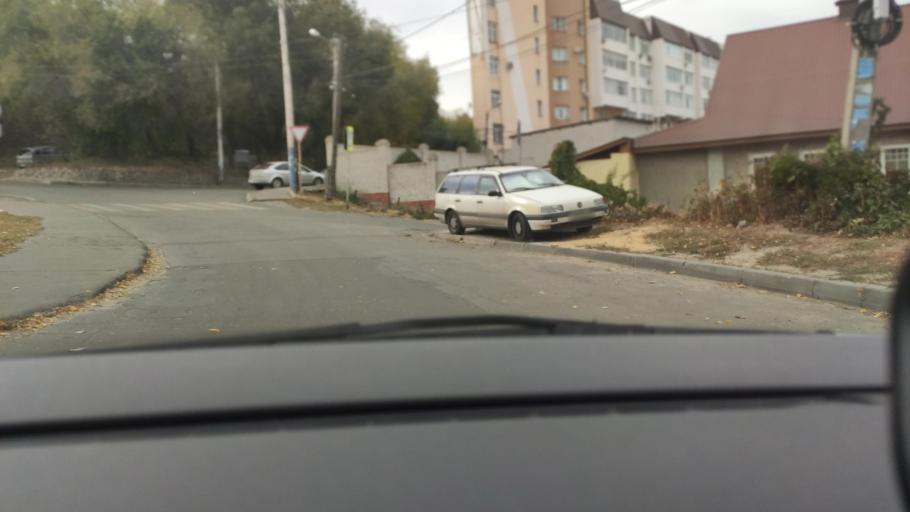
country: RU
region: Voronezj
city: Voronezh
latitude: 51.6652
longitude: 39.2153
